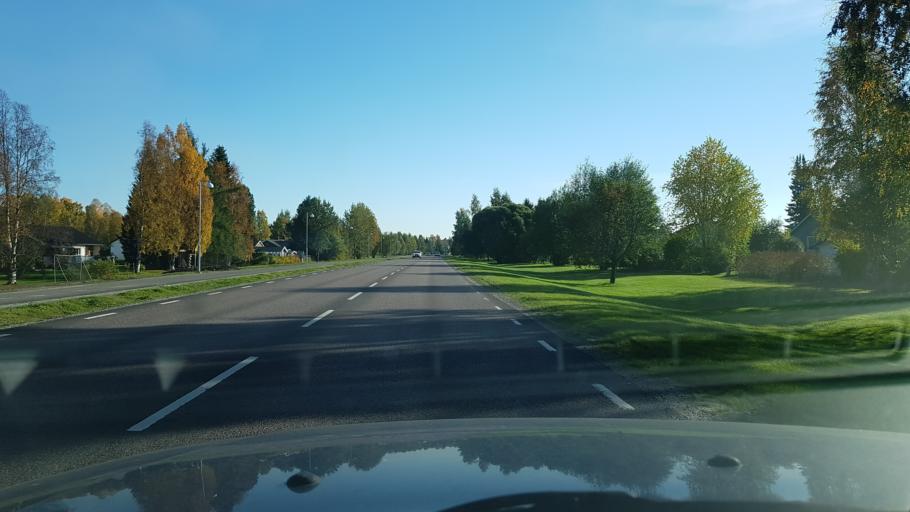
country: SE
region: Norrbotten
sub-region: Pitea Kommun
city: Pitea
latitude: 65.3237
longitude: 21.4531
